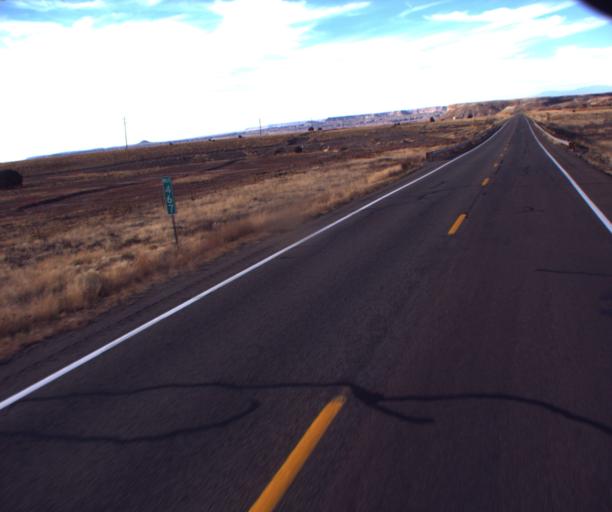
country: US
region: New Mexico
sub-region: San Juan County
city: Shiprock
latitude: 36.9036
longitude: -109.0687
